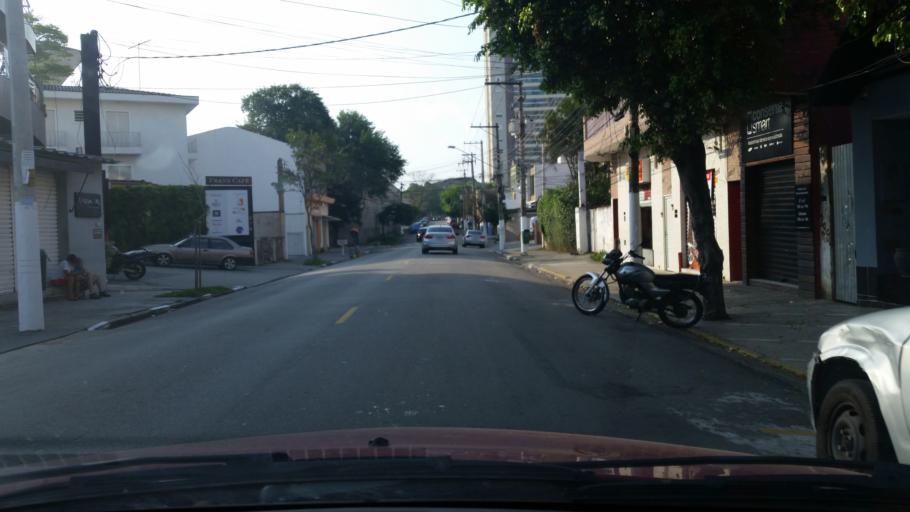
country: BR
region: Sao Paulo
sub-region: Osasco
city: Osasco
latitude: -23.5243
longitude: -46.7333
